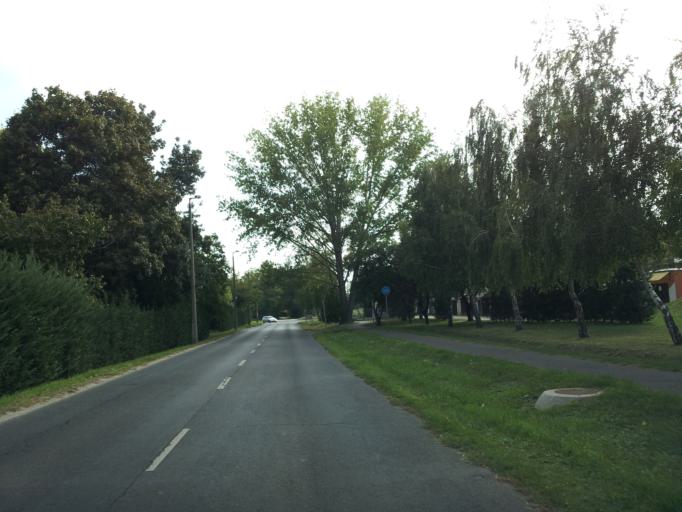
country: HU
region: Pest
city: Szazhalombatta
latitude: 47.3171
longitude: 18.9129
